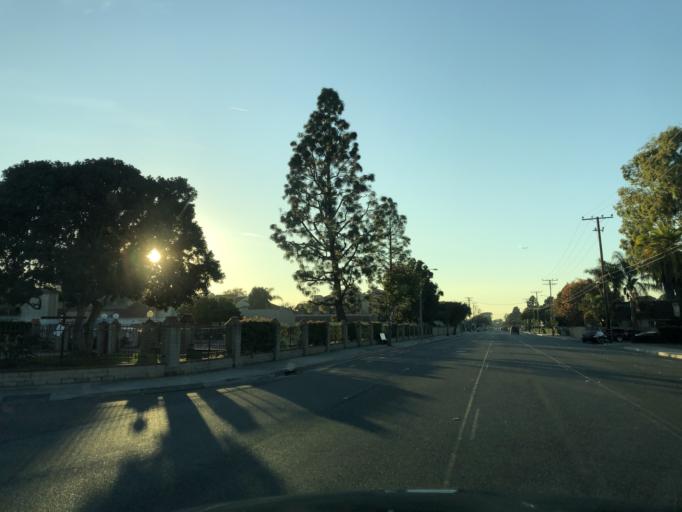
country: US
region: California
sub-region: Orange County
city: Westminster
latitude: 33.7226
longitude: -118.0436
